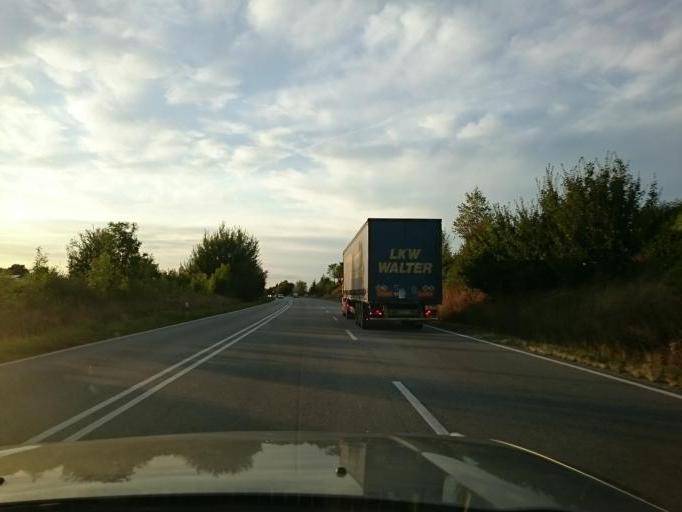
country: DE
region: Bavaria
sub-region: Lower Bavaria
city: Oberschneiding
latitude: 48.7698
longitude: 12.6582
